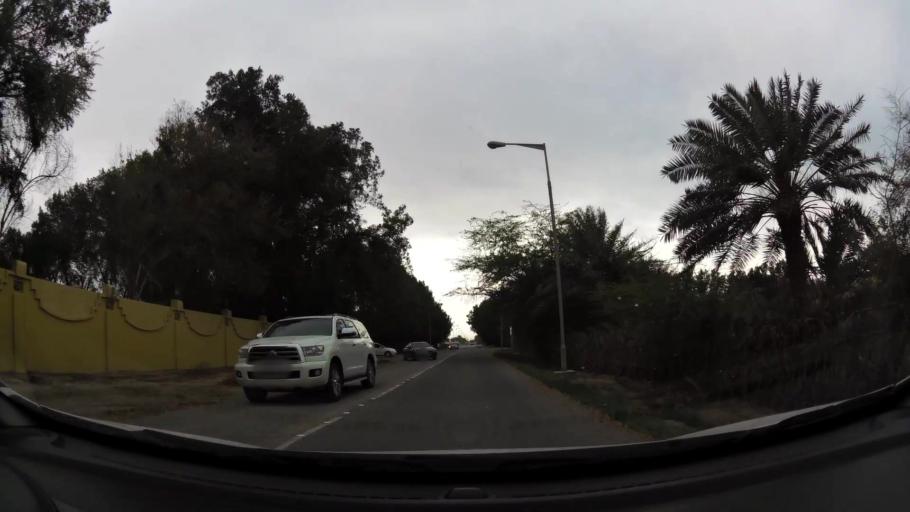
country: BH
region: Central Governorate
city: Madinat Hamad
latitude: 26.1530
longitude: 50.4635
